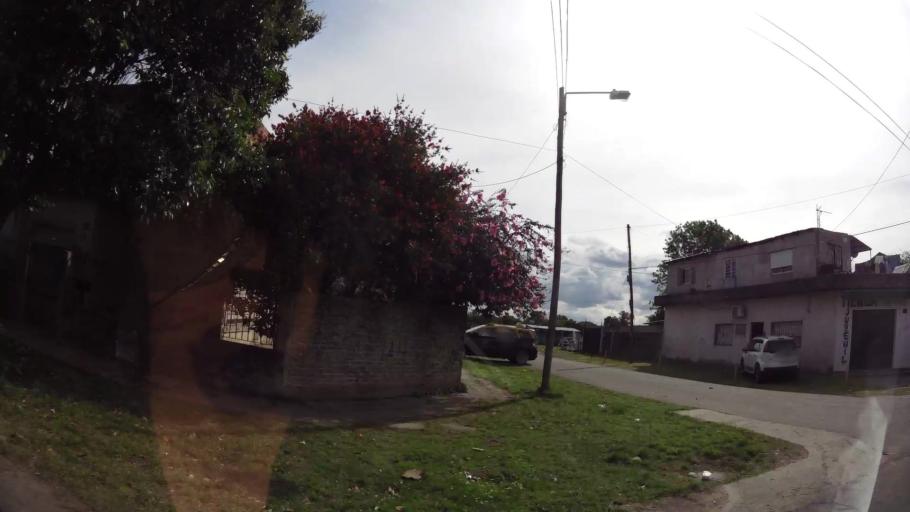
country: AR
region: Buenos Aires
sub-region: Partido de Quilmes
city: Quilmes
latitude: -34.7727
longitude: -58.2559
